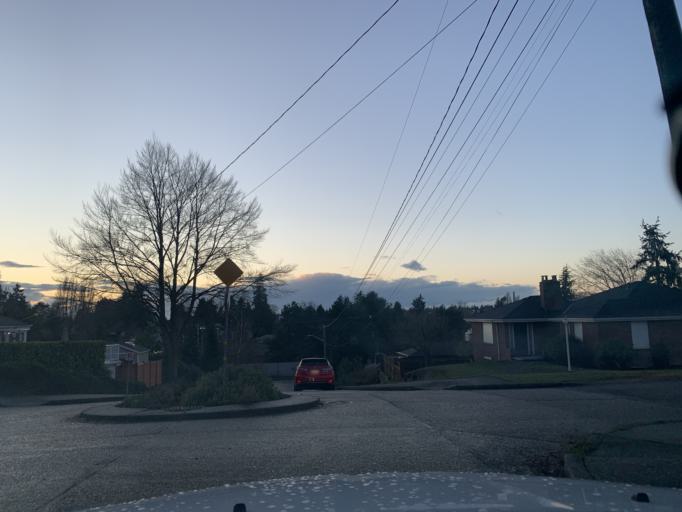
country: US
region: Washington
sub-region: King County
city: Shoreline
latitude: 47.6950
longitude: -122.3270
